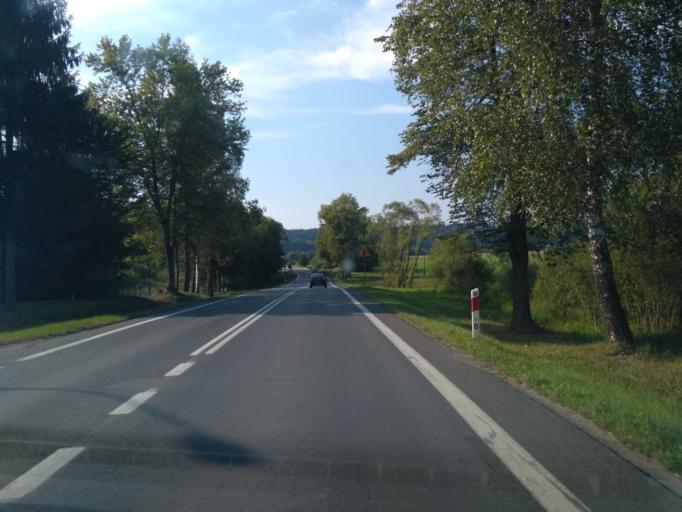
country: PL
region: Subcarpathian Voivodeship
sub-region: Powiat leski
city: Lesko
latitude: 49.4892
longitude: 22.3217
